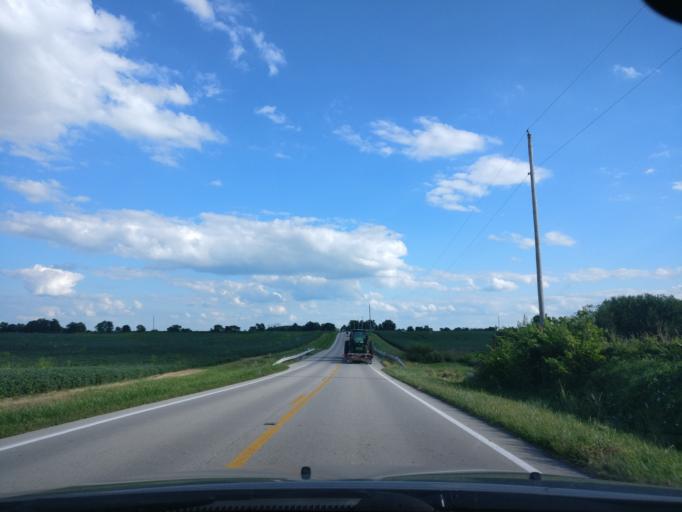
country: US
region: Ohio
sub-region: Clinton County
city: Sabina
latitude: 39.5523
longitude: -83.7163
